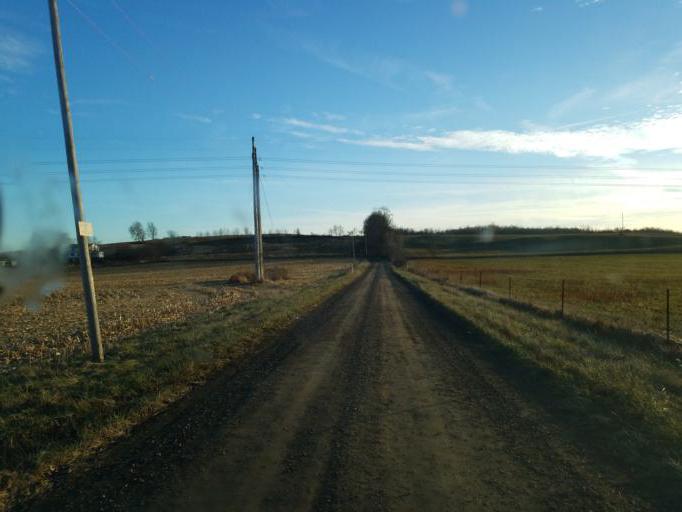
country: US
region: Ohio
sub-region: Muskingum County
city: Dresden
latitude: 40.0991
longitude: -81.9741
